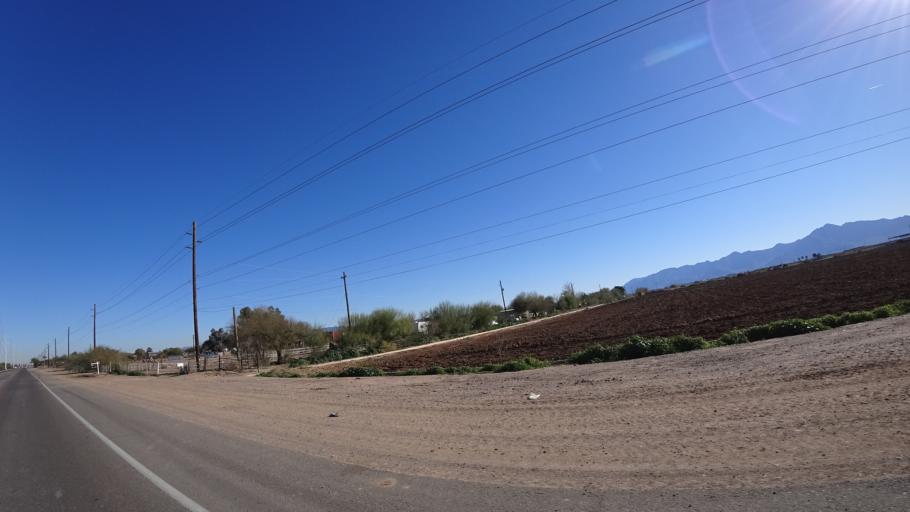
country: US
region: Arizona
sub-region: Maricopa County
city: Tolleson
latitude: 33.4084
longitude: -112.2177
